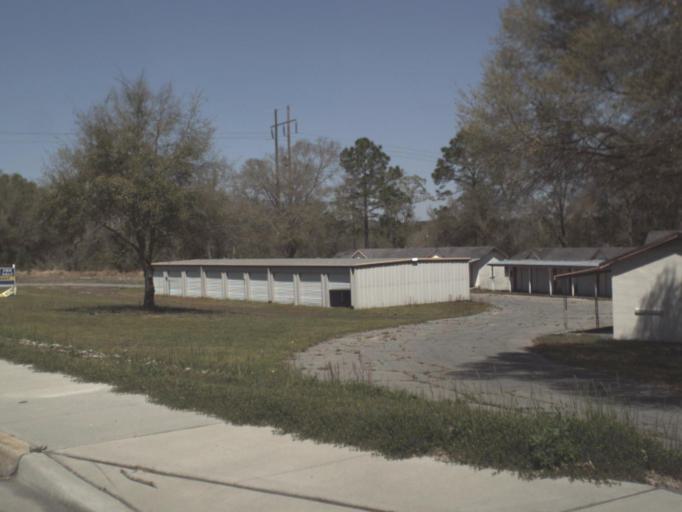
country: US
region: Florida
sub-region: Walton County
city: DeFuniak Springs
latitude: 30.7249
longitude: -86.1267
